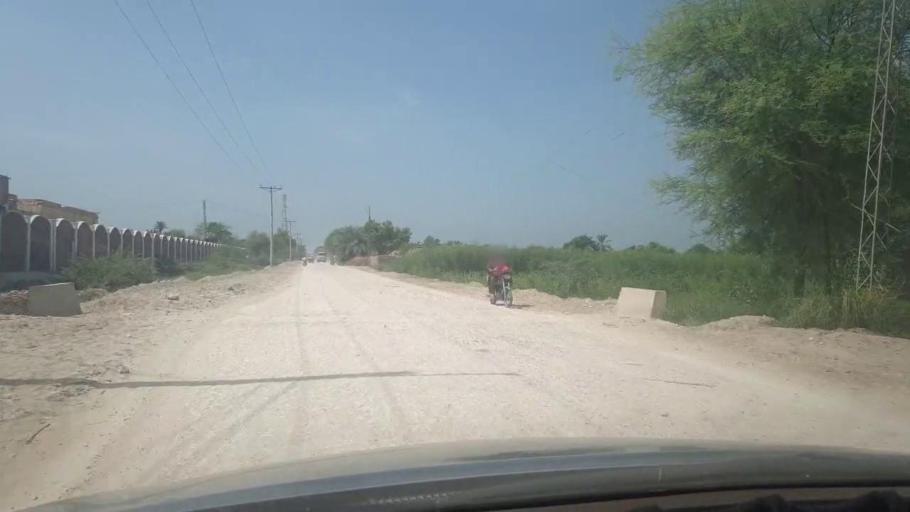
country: PK
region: Sindh
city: Ranipur
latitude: 27.2845
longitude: 68.6026
